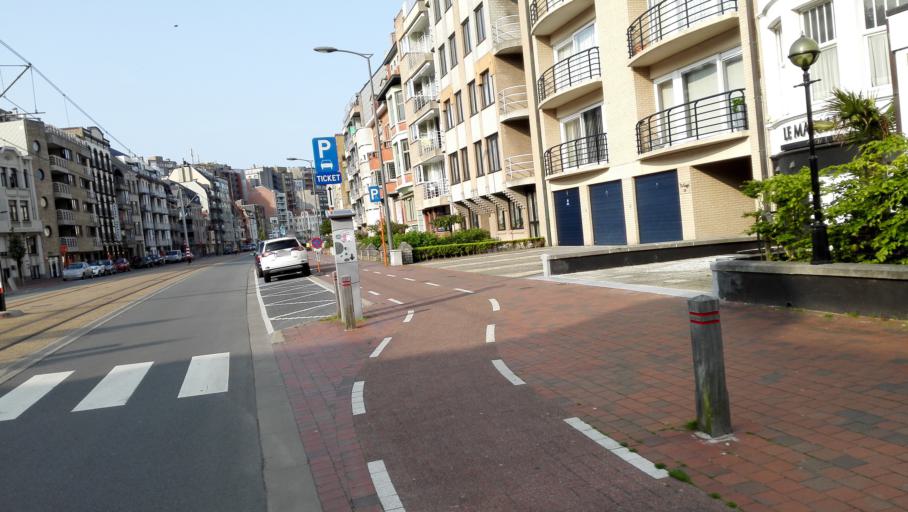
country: BE
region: Flanders
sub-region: Provincie West-Vlaanderen
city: Blankenberge
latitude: 51.3151
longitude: 3.1331
